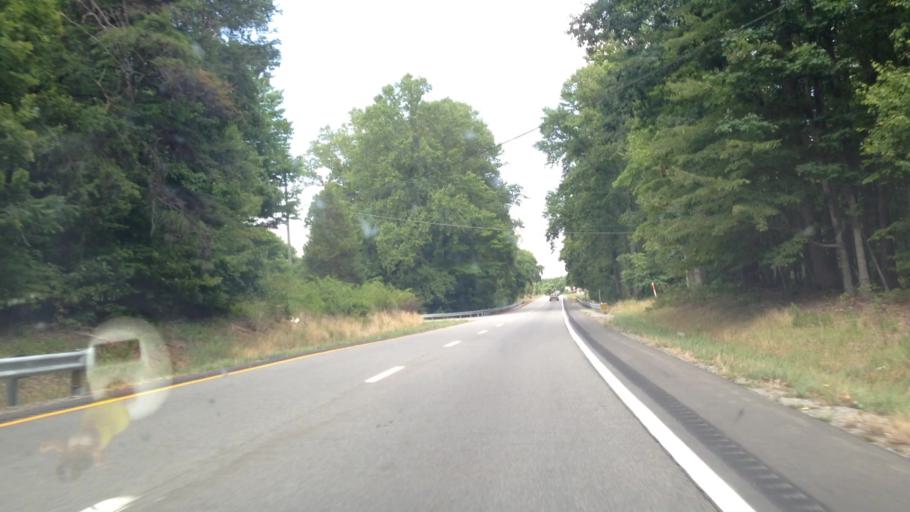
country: US
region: North Carolina
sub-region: Rockingham County
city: Stoneville
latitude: 36.5580
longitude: -79.8876
